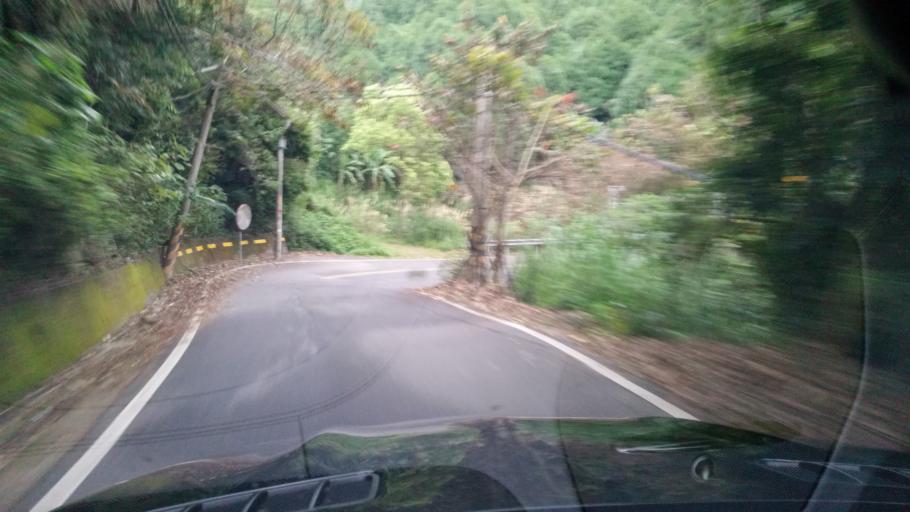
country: TW
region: Taiwan
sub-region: Miaoli
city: Miaoli
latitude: 24.5830
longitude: 120.8992
